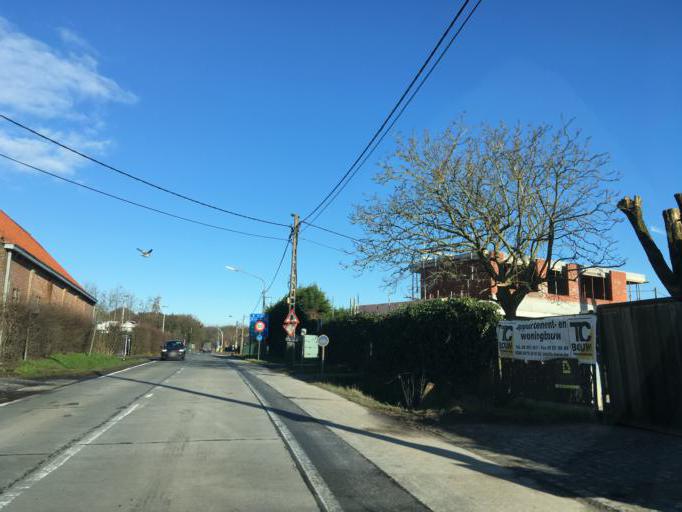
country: BE
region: Flanders
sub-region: Provincie West-Vlaanderen
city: Roeselare
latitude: 50.9210
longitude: 3.1405
